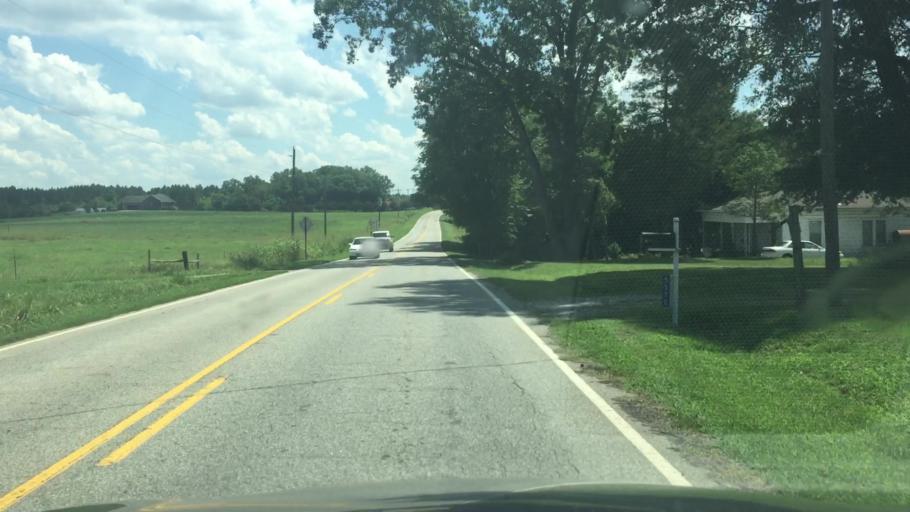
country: US
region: North Carolina
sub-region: Rowan County
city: China Grove
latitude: 35.6462
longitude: -80.6373
